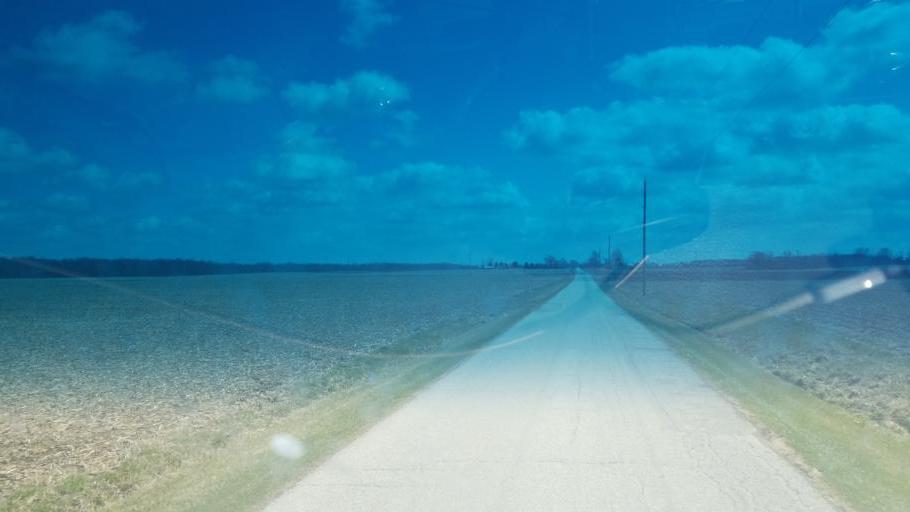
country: US
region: Ohio
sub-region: Crawford County
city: Bucyrus
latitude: 40.8485
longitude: -83.0591
